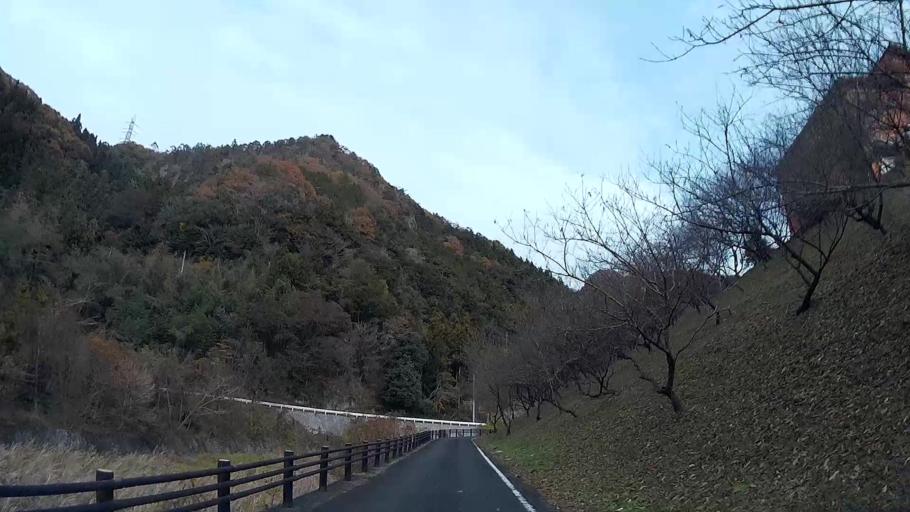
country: JP
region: Saitama
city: Chichibu
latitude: 36.0593
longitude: 138.9664
